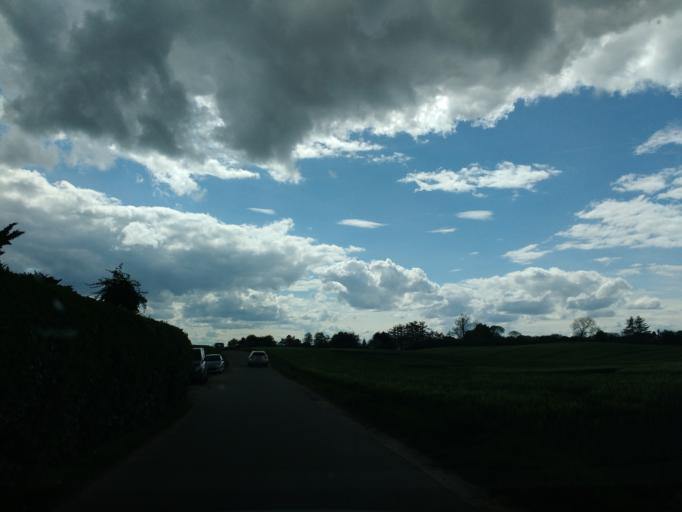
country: DE
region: Schleswig-Holstein
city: Loose
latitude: 54.4986
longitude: 9.8629
